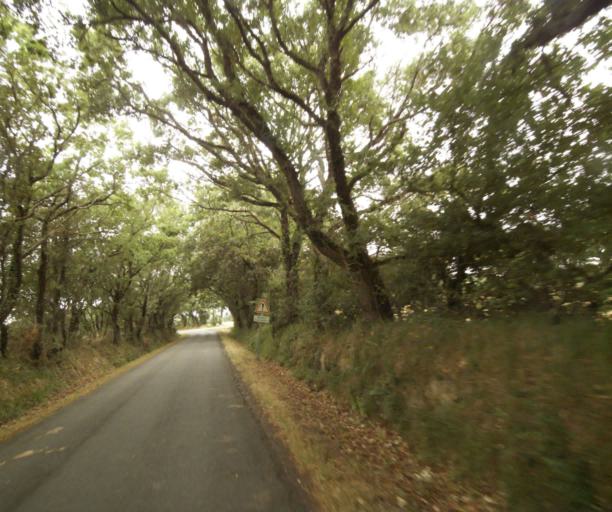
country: FR
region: Pays de la Loire
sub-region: Departement de la Vendee
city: Chateau-d'Olonne
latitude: 46.4900
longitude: -1.6881
